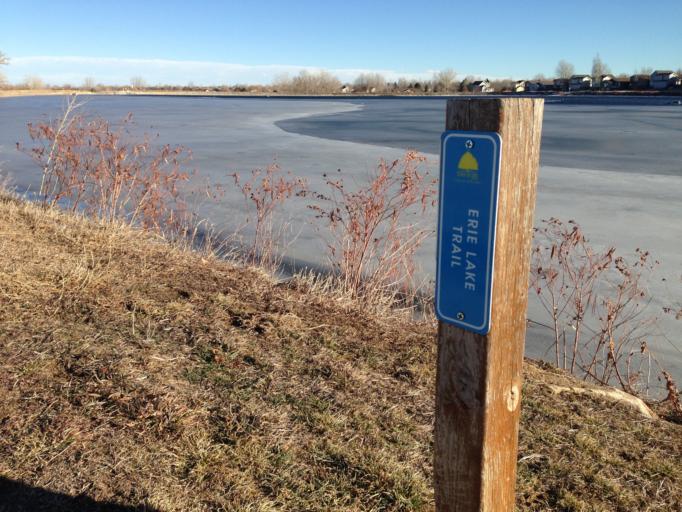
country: US
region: Colorado
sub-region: Boulder County
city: Lafayette
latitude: 40.0199
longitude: -105.1011
